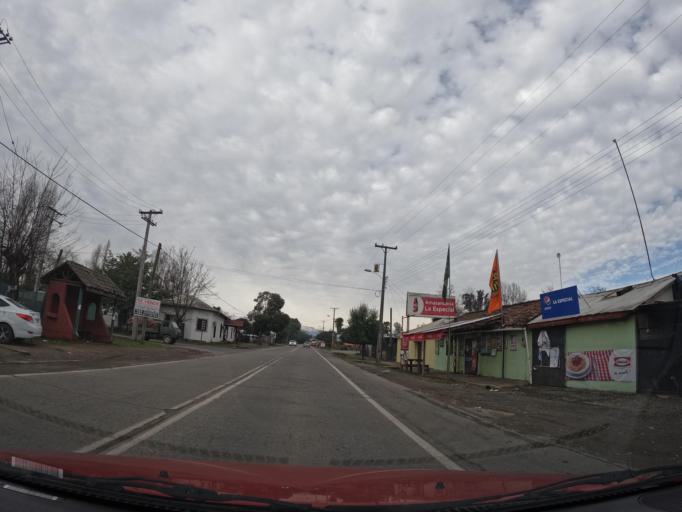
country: CL
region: Maule
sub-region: Provincia de Linares
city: Linares
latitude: -35.8651
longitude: -71.5560
